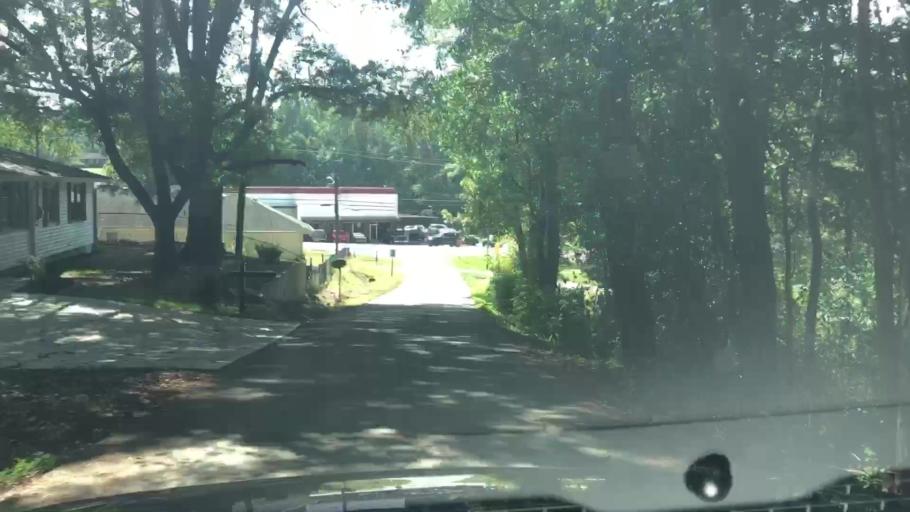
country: US
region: Georgia
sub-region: Paulding County
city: Dallas
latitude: 33.9267
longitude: -84.8343
